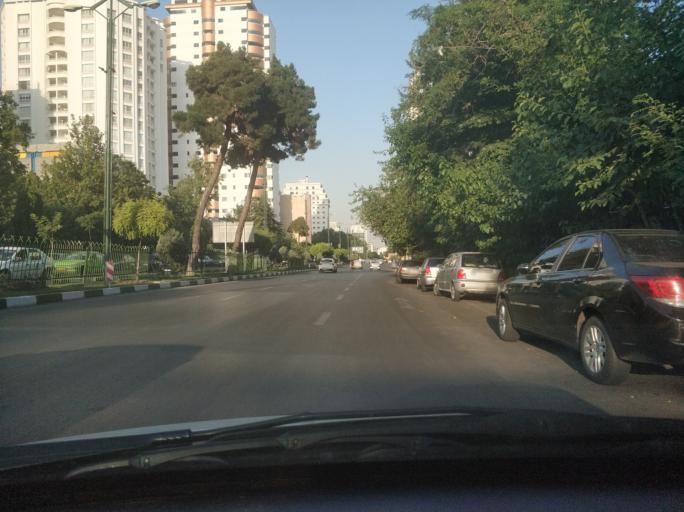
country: IR
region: Tehran
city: Tajrish
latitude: 35.8016
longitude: 51.4589
